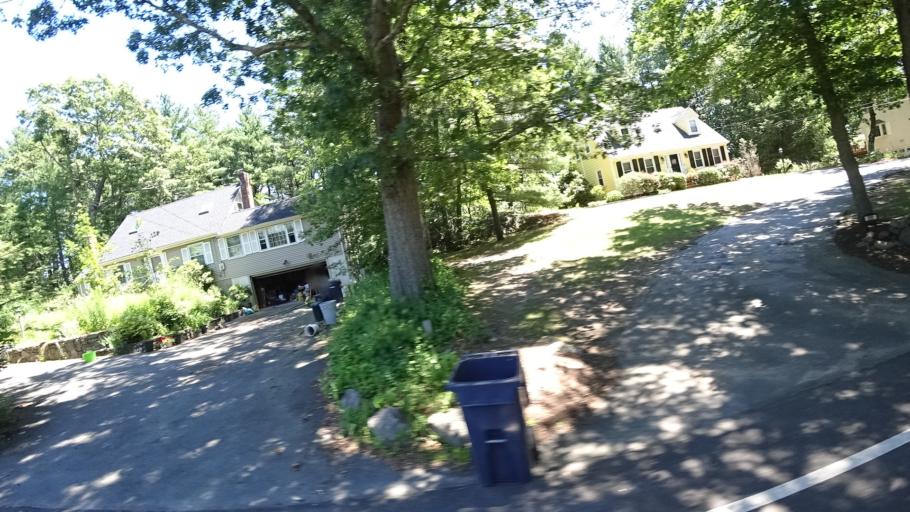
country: US
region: Massachusetts
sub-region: Norfolk County
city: Dedham
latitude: 42.2246
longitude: -71.1552
